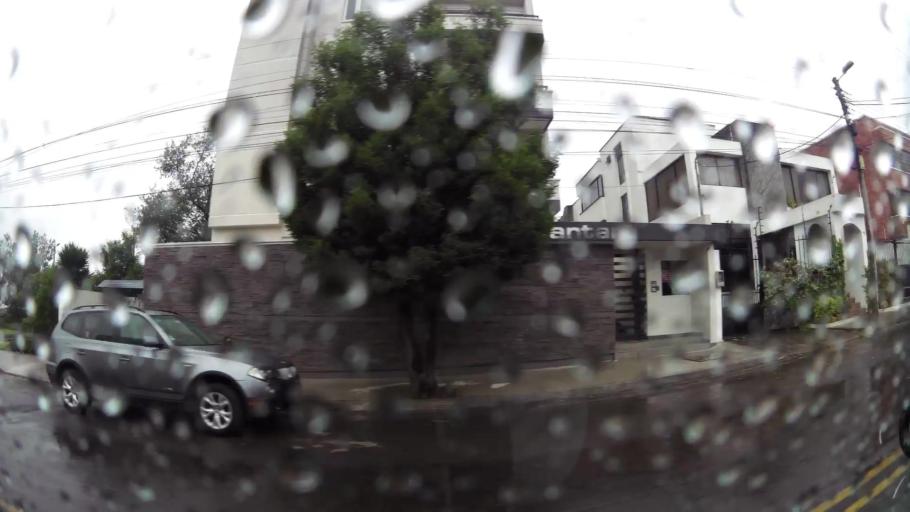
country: EC
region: Pichincha
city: Quito
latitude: -0.1008
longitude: -78.4977
